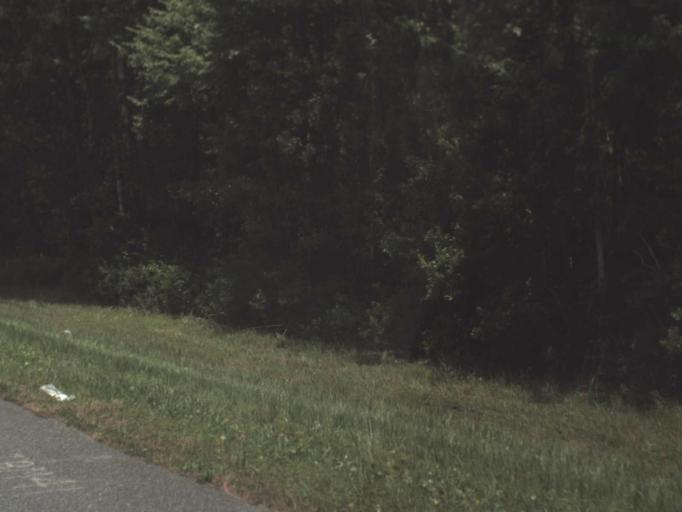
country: US
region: Florida
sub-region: Union County
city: Lake Butler
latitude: 30.1043
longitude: -82.2167
